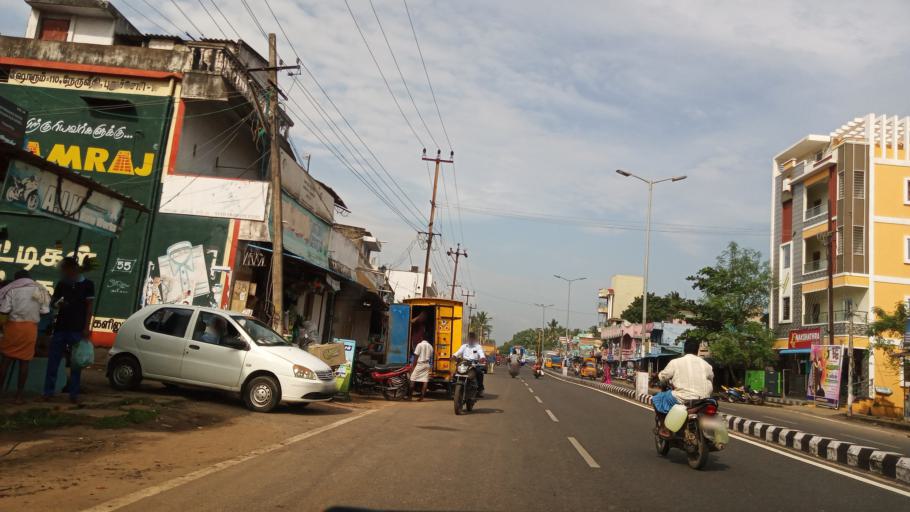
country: IN
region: Tamil Nadu
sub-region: Villupuram
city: Auroville
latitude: 12.0424
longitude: 79.8689
